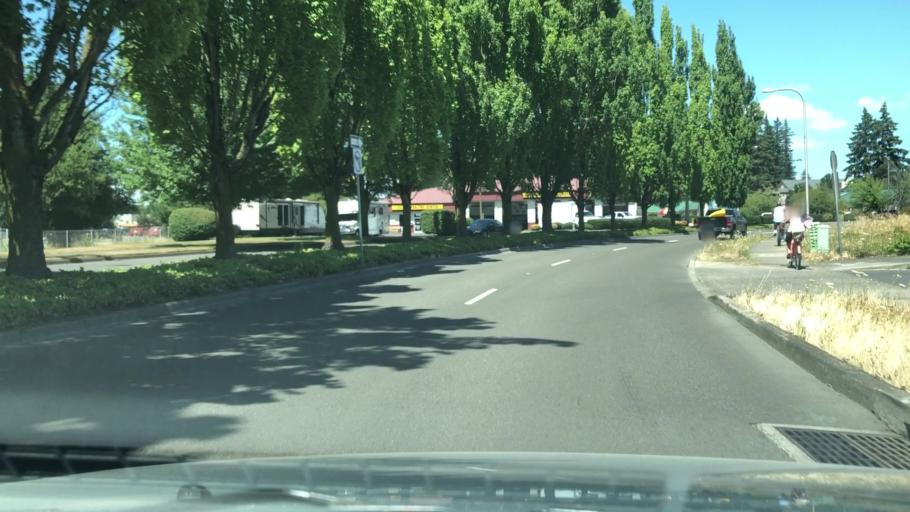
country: US
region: Oregon
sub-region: Clackamas County
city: Wilsonville
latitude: 45.3079
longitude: -122.7684
